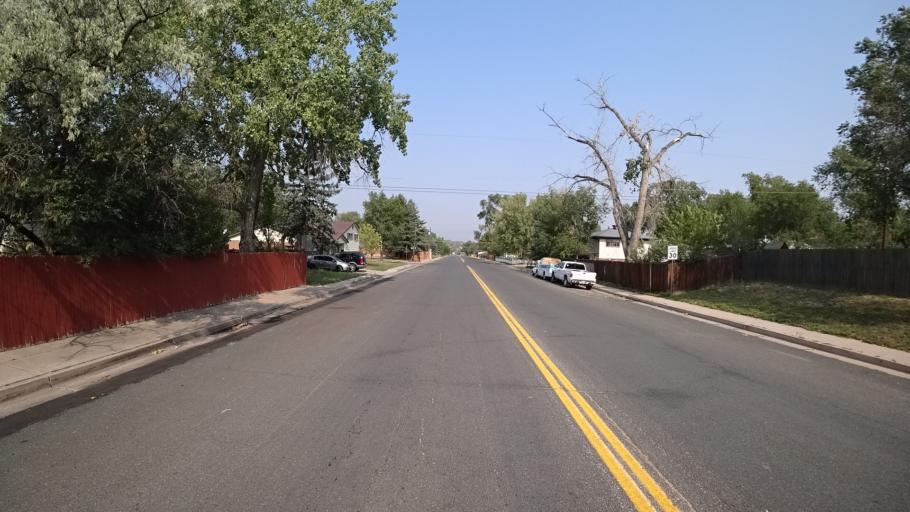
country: US
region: Colorado
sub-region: El Paso County
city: Stratmoor
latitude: 38.8109
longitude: -104.7759
